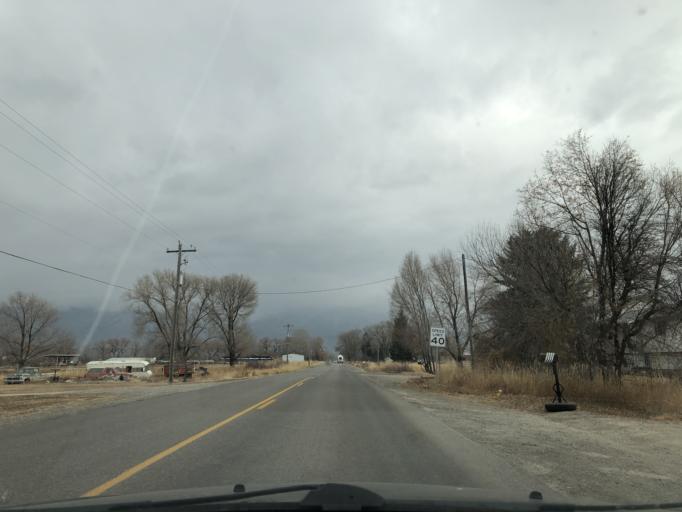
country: US
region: Utah
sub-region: Cache County
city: Nibley
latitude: 41.6752
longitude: -111.8809
